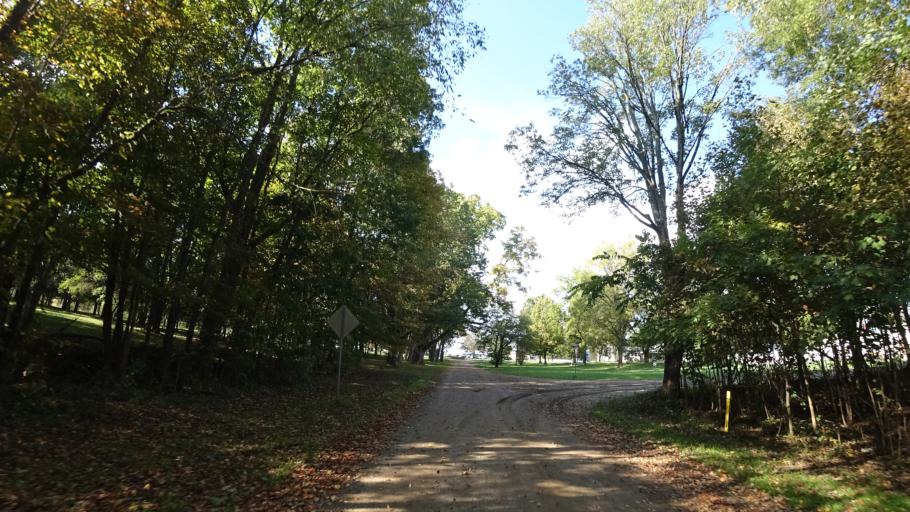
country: US
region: Michigan
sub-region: Saint Joseph County
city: Three Rivers
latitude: 41.9534
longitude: -85.6406
